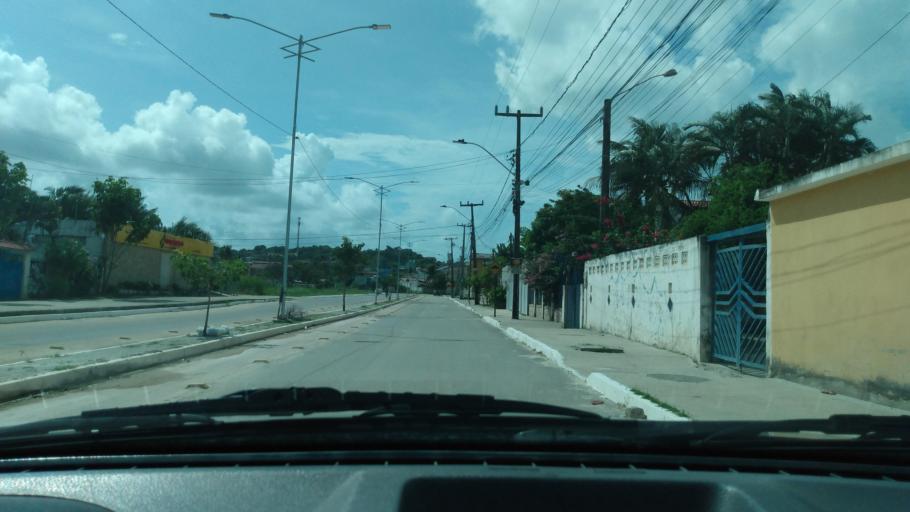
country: BR
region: Pernambuco
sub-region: Cabo De Santo Agostinho
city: Cabo
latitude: -8.3228
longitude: -34.9531
